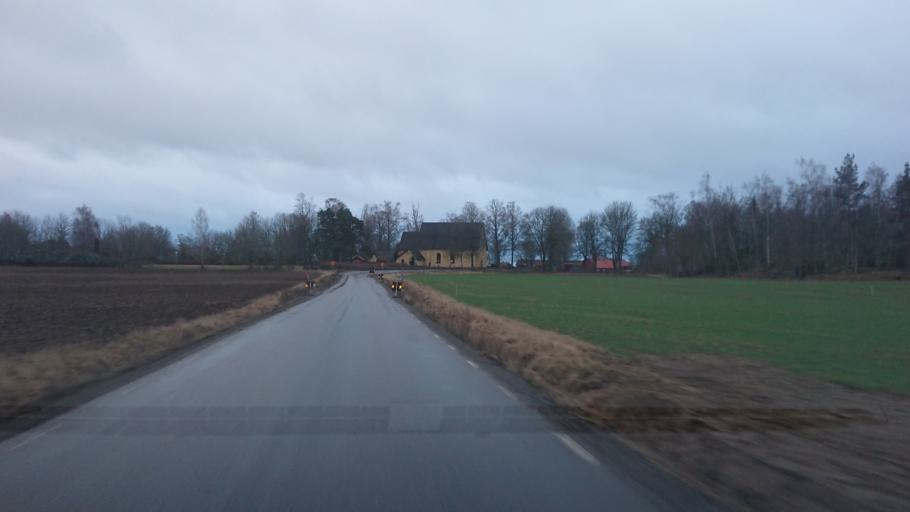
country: SE
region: Uppsala
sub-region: Uppsala Kommun
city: Gamla Uppsala
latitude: 59.9578
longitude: 17.6054
